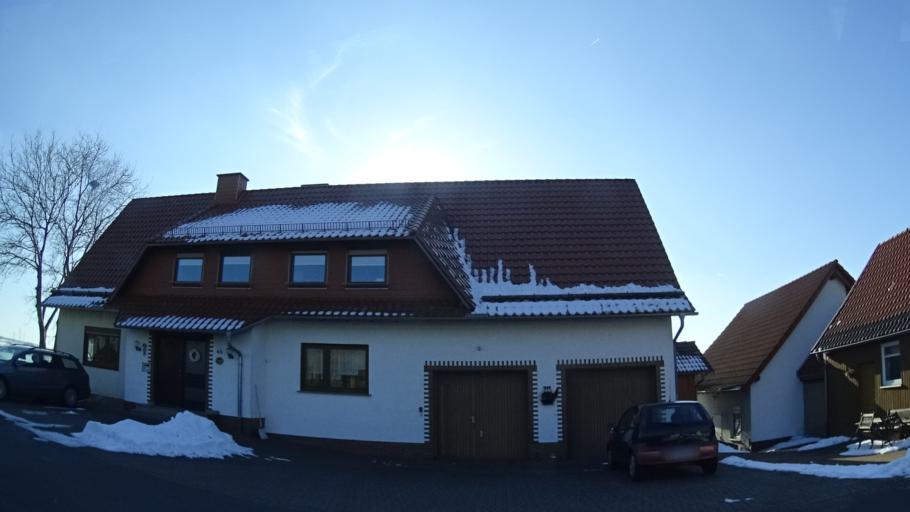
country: DE
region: Hesse
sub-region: Regierungsbezirk Kassel
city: Kalbach
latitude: 50.3902
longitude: 9.6405
